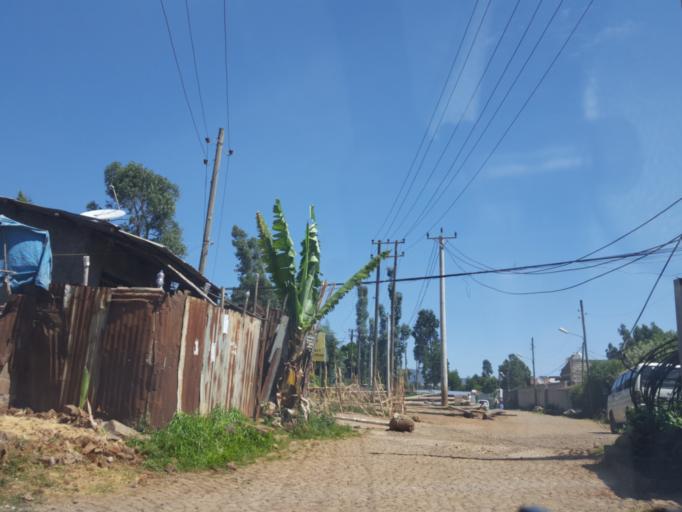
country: ET
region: Adis Abeba
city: Addis Ababa
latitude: 9.0575
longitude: 38.7479
